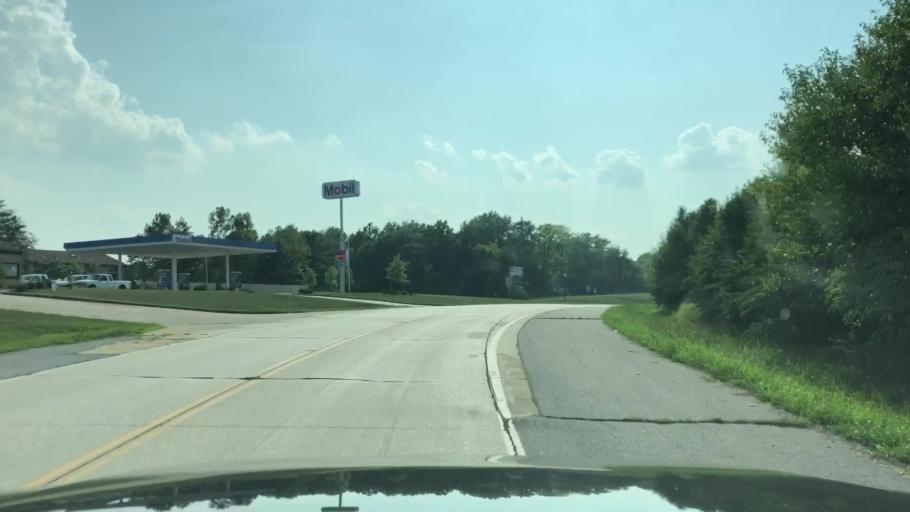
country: US
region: Missouri
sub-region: Saint Charles County
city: Lake Saint Louis
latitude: 38.8041
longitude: -90.8066
